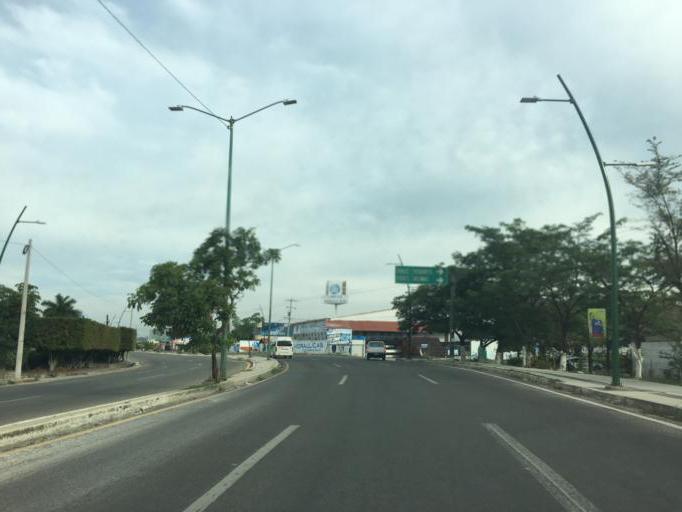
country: MX
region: Chiapas
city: Tuxtla Gutierrez
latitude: 16.7655
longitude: -93.1632
